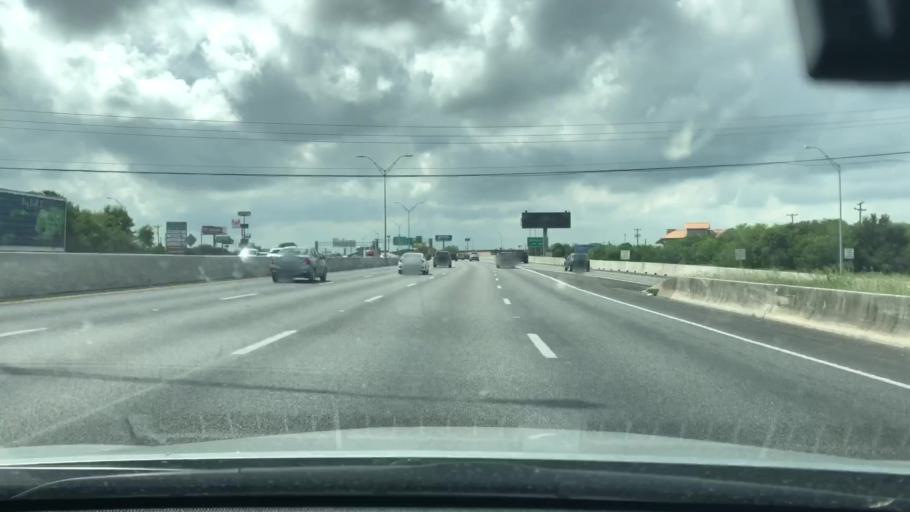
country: US
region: Texas
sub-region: Bexar County
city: Windcrest
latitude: 29.5186
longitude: -98.3957
